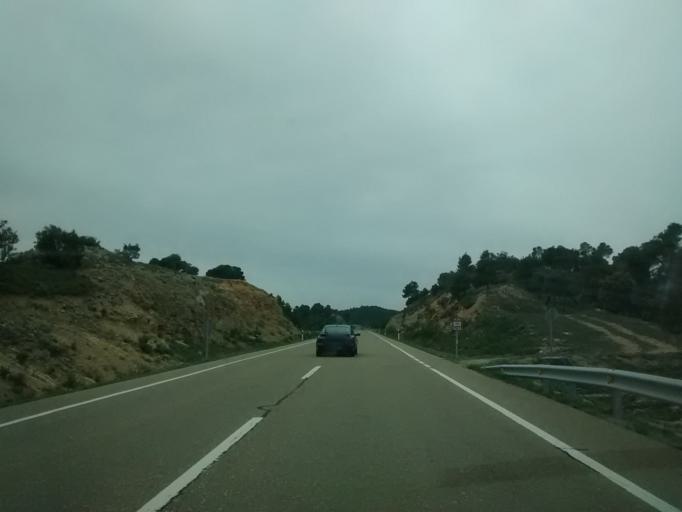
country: ES
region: Aragon
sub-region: Provincia de Teruel
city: Fornoles
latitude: 40.8658
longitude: -0.0305
